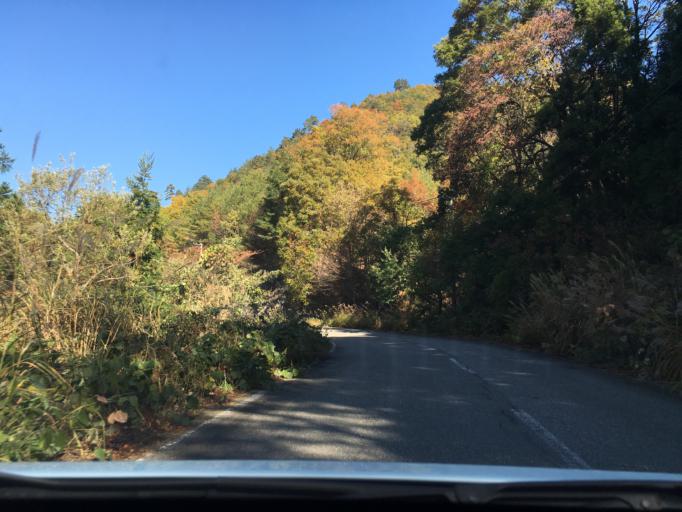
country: JP
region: Fukushima
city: Inawashiro
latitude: 37.4476
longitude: 139.9679
